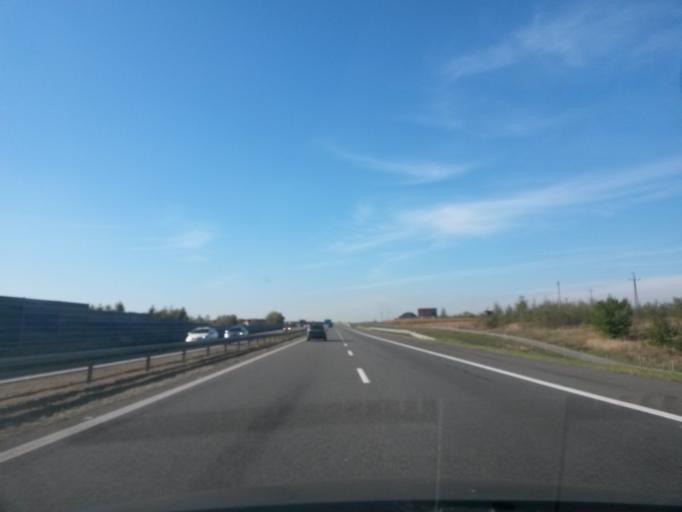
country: PL
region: Opole Voivodeship
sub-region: Powiat krapkowicki
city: Krapkowice
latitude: 50.5192
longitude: 17.9473
